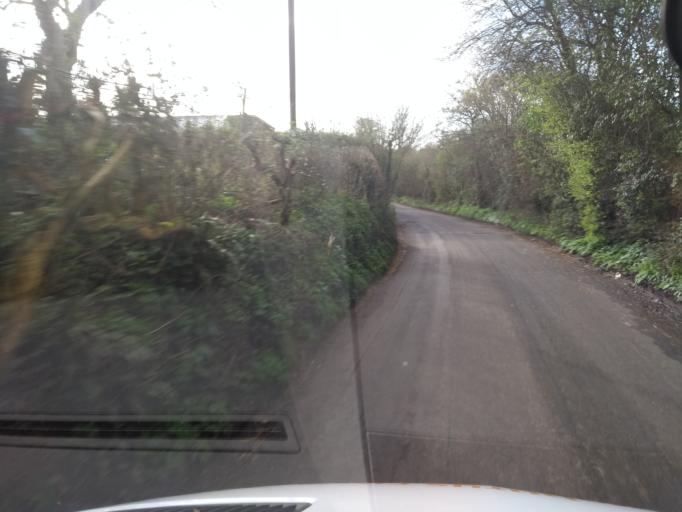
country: GB
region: England
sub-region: Somerset
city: Street
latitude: 51.1248
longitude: -2.8231
